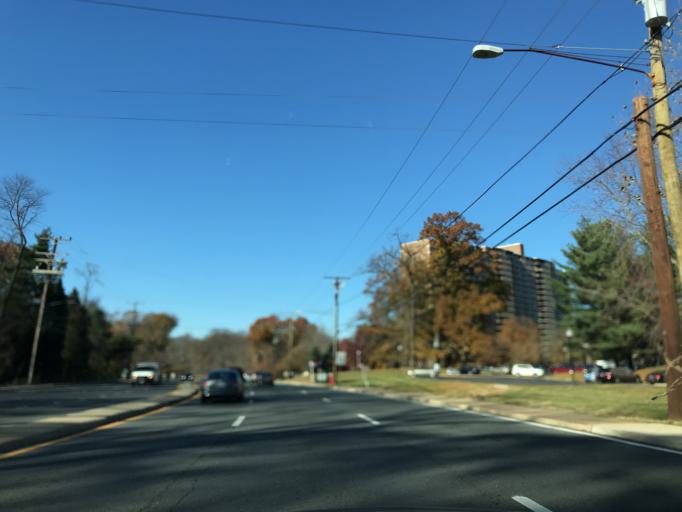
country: US
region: Maryland
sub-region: Montgomery County
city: Kemp Mill
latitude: 39.0359
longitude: -77.0266
